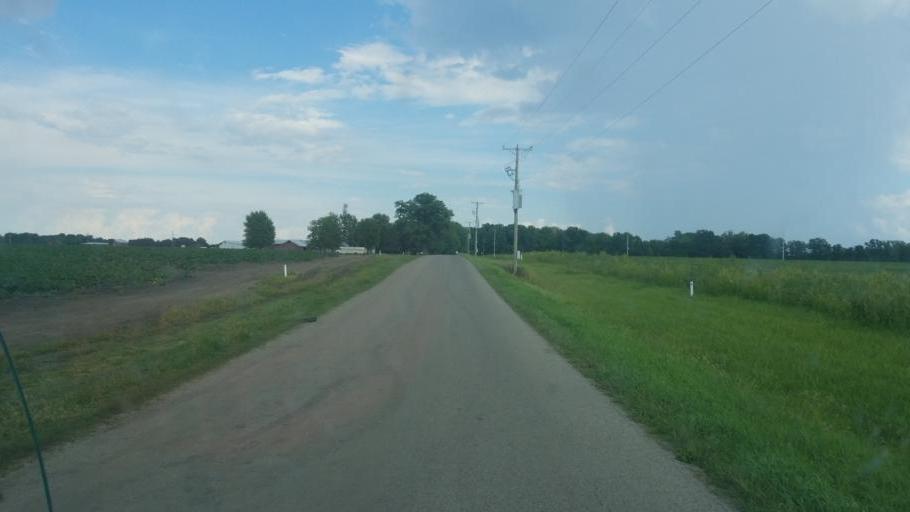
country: US
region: Ohio
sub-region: Huron County
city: Plymouth
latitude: 41.0185
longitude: -82.6938
